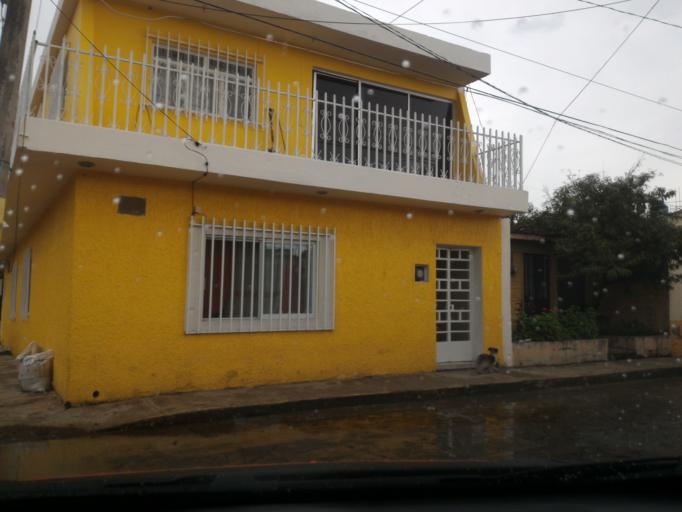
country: MX
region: Jalisco
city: San Andres Ixtlan
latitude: 19.8204
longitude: -103.4660
